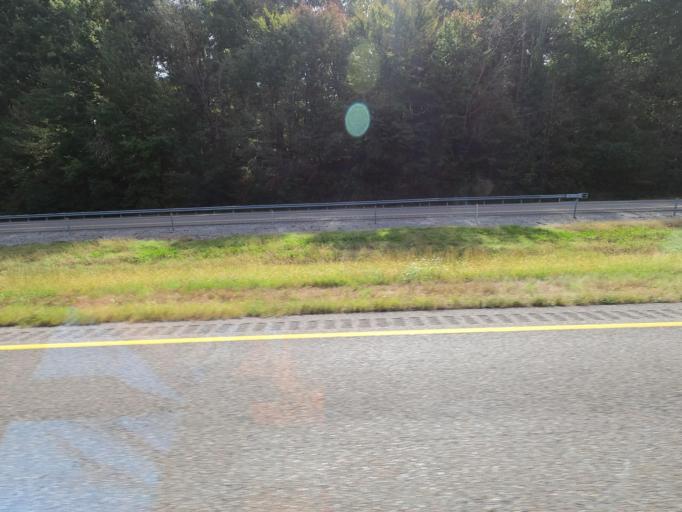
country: US
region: Tennessee
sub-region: Humphreys County
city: New Johnsonville
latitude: 35.8740
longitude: -87.8584
